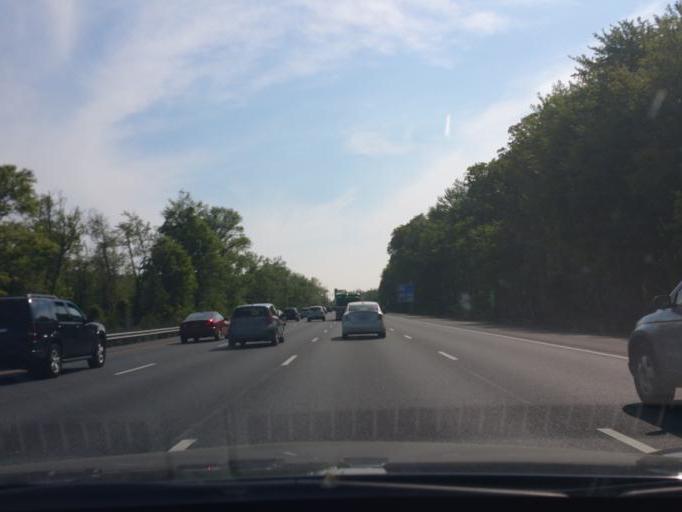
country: US
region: Maryland
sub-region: Baltimore County
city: White Marsh
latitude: 39.4034
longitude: -76.4237
